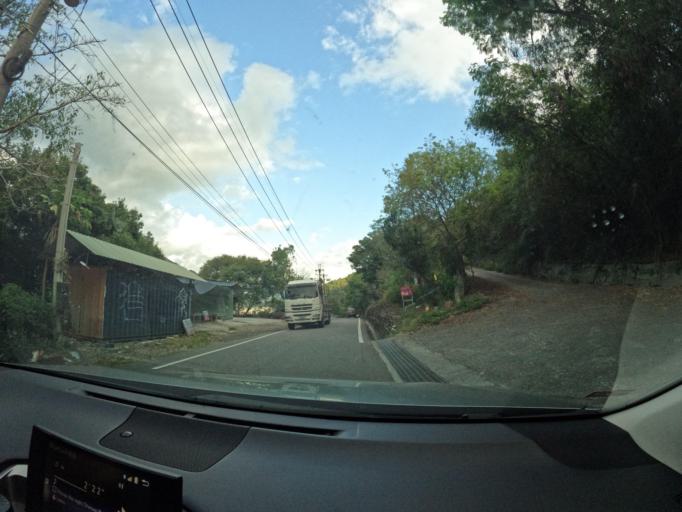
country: TW
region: Taiwan
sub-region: Taitung
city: Taitung
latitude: 23.1298
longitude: 121.1509
